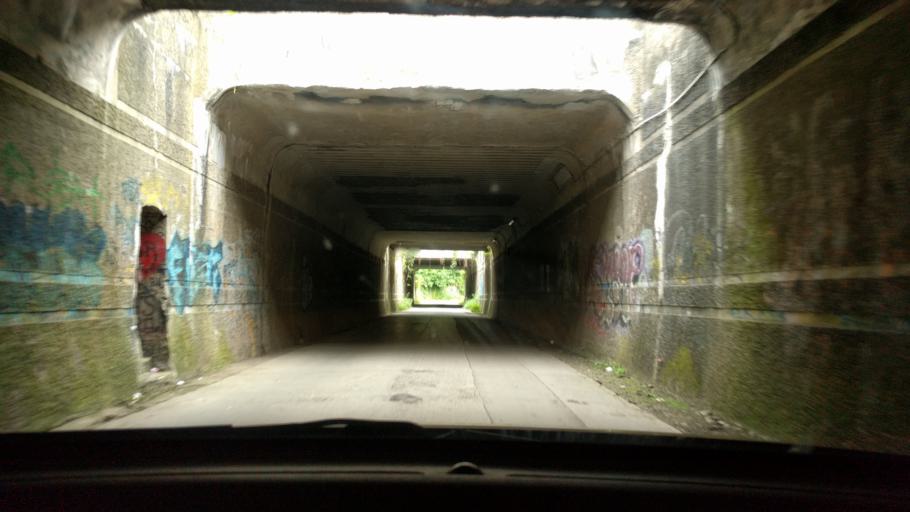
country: DE
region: North Rhine-Westphalia
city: Witten
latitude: 51.4790
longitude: 7.3280
